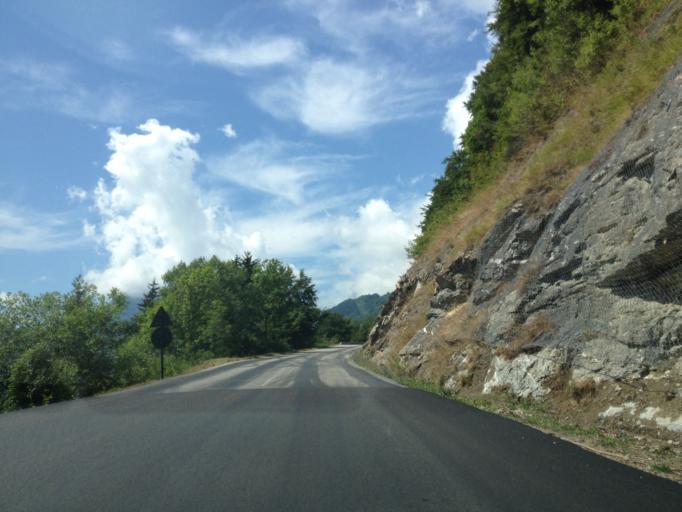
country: FR
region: Rhone-Alpes
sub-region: Departement de la Savoie
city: Salins-les-Thermes
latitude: 45.4529
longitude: 6.5033
